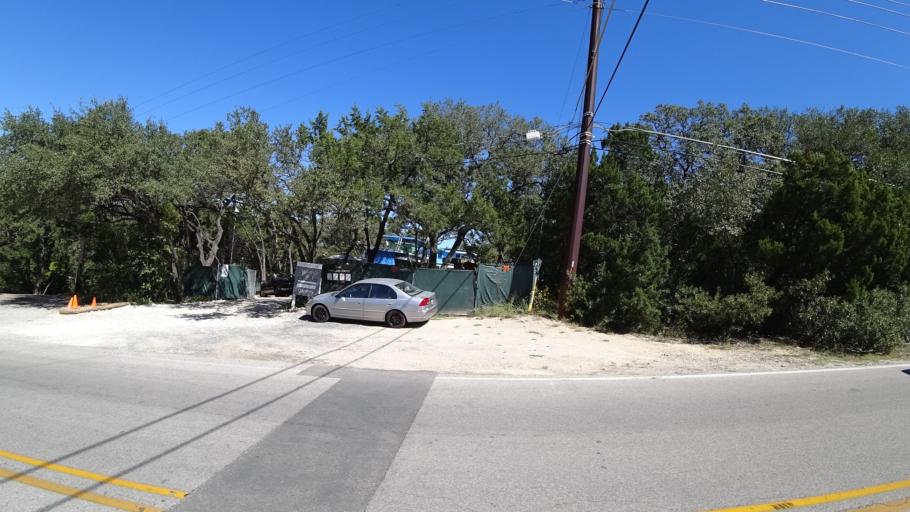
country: US
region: Texas
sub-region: Travis County
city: West Lake Hills
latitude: 30.3273
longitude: -97.7811
